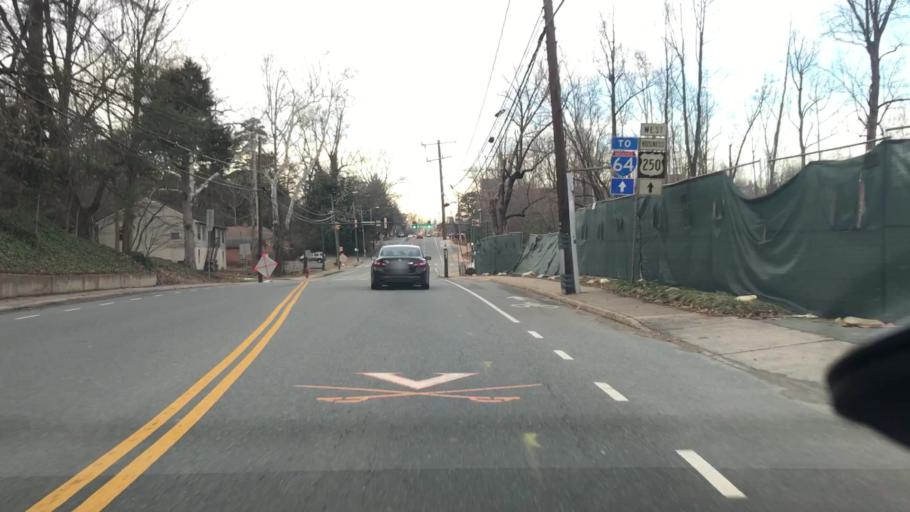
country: US
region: Virginia
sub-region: City of Charlottesville
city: Charlottesville
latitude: 38.0403
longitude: -78.5073
